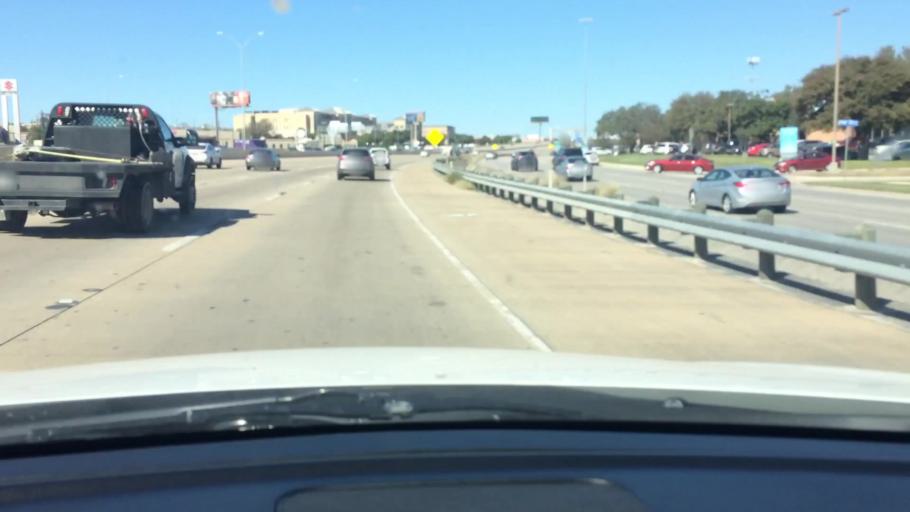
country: US
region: Texas
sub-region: Bexar County
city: Balcones Heights
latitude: 29.4867
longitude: -98.5431
